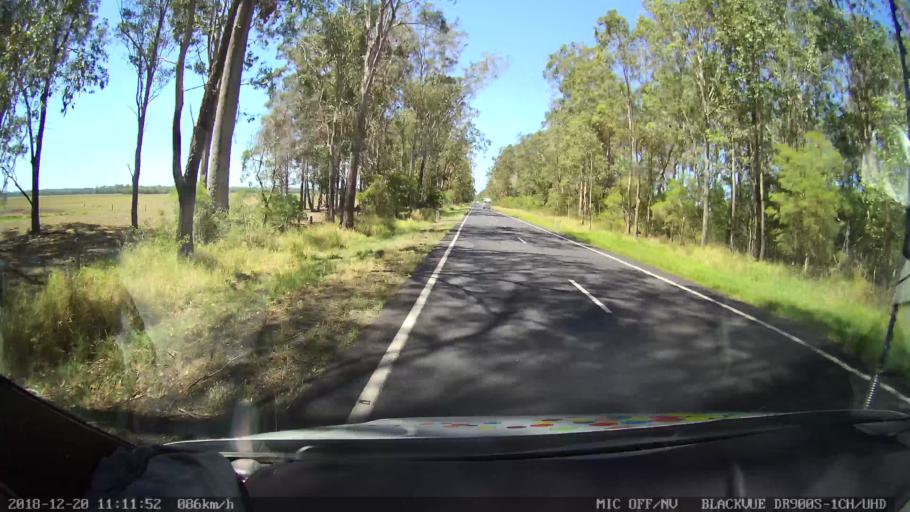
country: AU
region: New South Wales
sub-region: Richmond Valley
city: Casino
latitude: -28.9665
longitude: 153.0126
